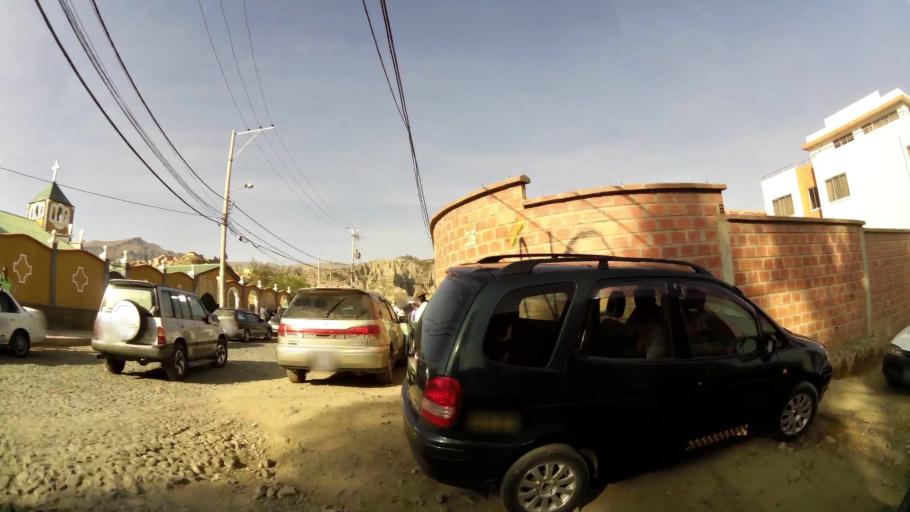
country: BO
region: La Paz
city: La Paz
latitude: -16.5167
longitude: -68.0845
